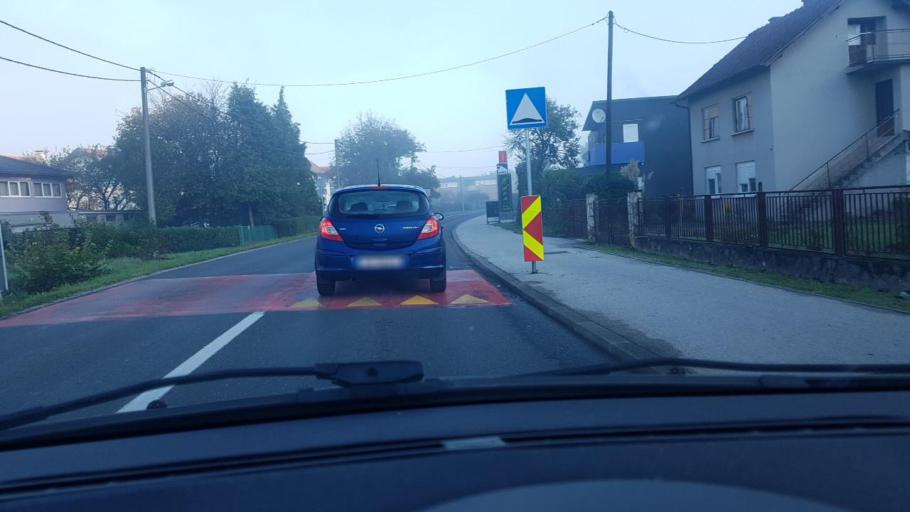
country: HR
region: Grad Zagreb
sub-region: Sesvete
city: Sesvete
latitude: 45.8436
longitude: 16.1089
